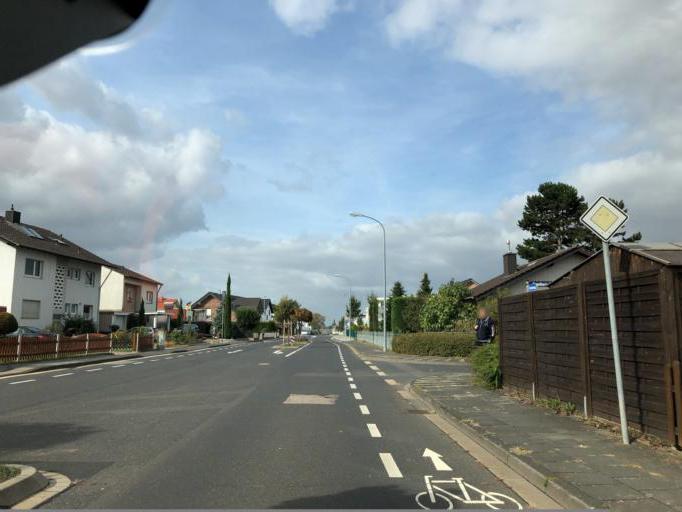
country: DE
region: North Rhine-Westphalia
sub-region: Regierungsbezirk Koln
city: Rheinbach
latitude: 50.6505
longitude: 6.8747
